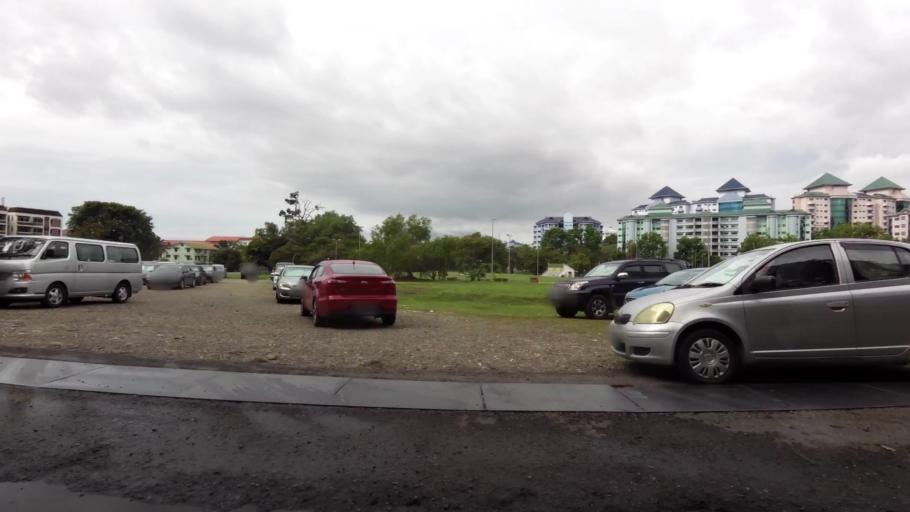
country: BN
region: Brunei and Muara
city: Bandar Seri Begawan
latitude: 4.9060
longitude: 114.9361
